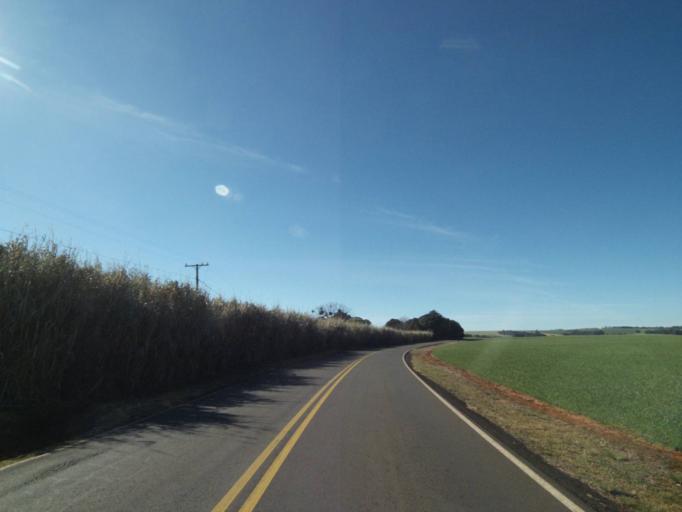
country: BR
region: Parana
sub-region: Tibagi
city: Tibagi
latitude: -24.5201
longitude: -50.3314
